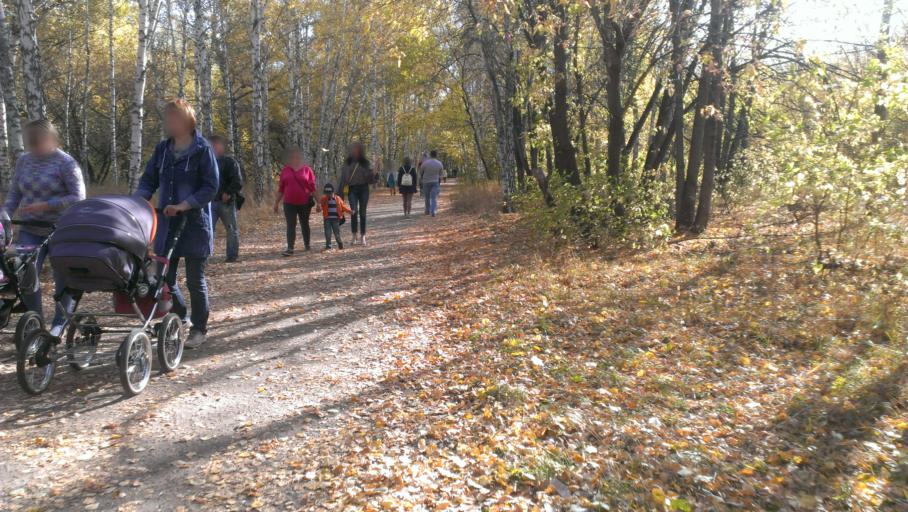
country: RU
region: Altai Krai
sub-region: Gorod Barnaulskiy
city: Barnaul
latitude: 53.3605
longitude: 83.6851
